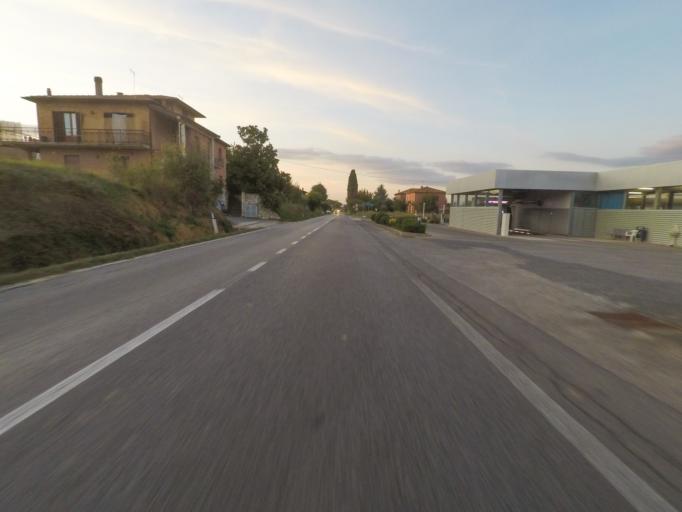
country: IT
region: Tuscany
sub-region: Provincia di Siena
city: Torrita di Siena
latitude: 43.1788
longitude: 11.7718
